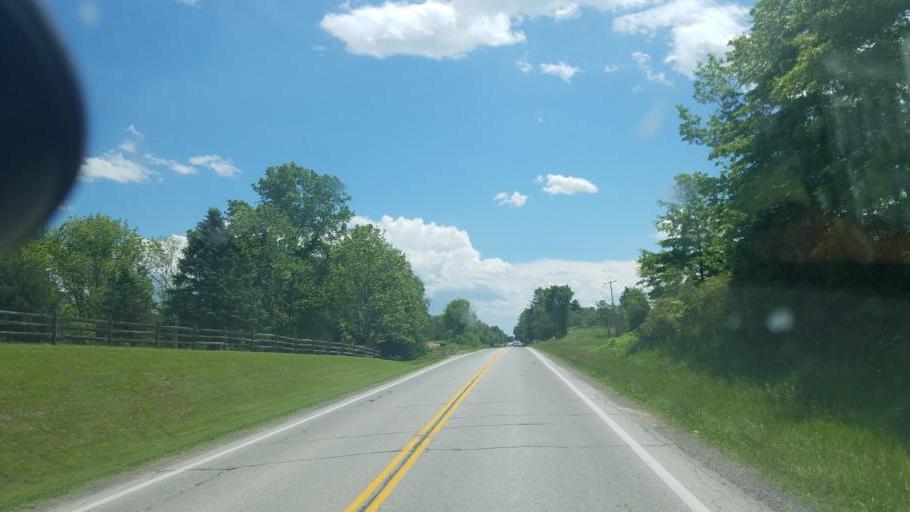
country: US
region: Ohio
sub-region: Geauga County
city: Middlefield
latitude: 41.4530
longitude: -80.9549
